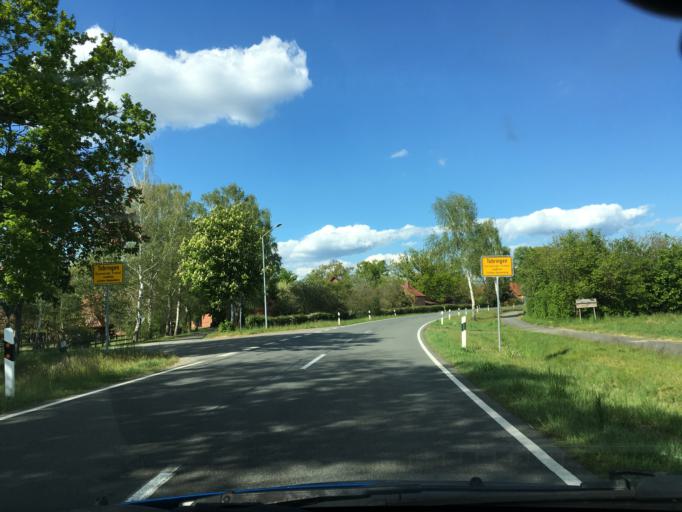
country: DE
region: Lower Saxony
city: Trebel
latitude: 52.9823
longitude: 11.2947
